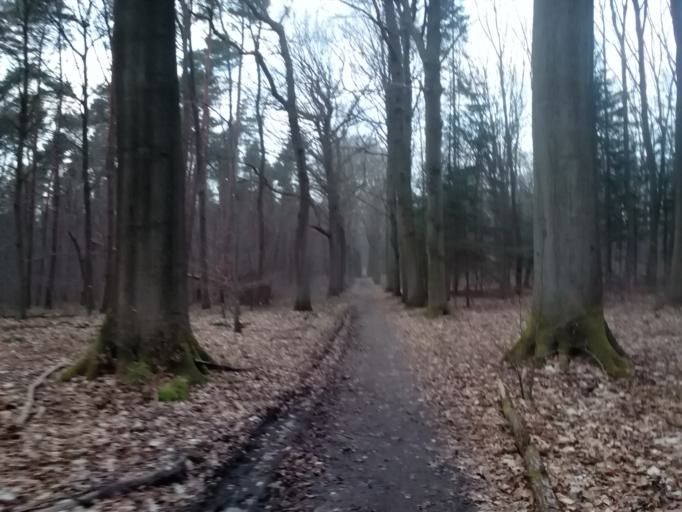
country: BE
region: Flanders
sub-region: Provincie Vlaams-Brabant
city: Oud-Heverlee
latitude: 50.8390
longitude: 4.6831
